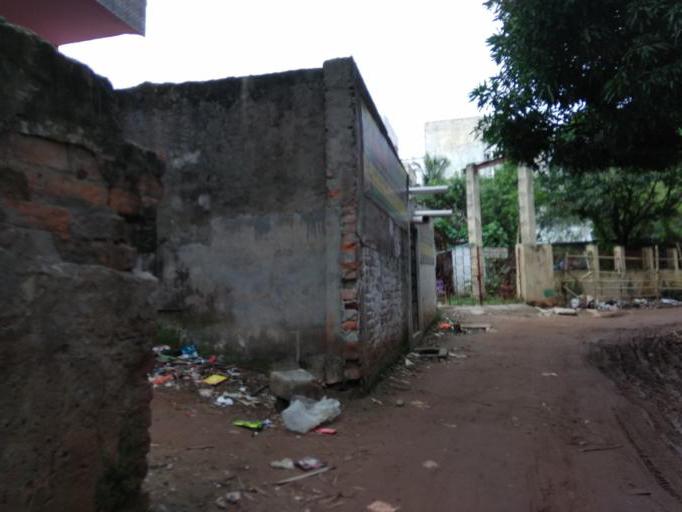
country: BD
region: Dhaka
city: Tungi
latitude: 23.8152
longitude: 90.3723
